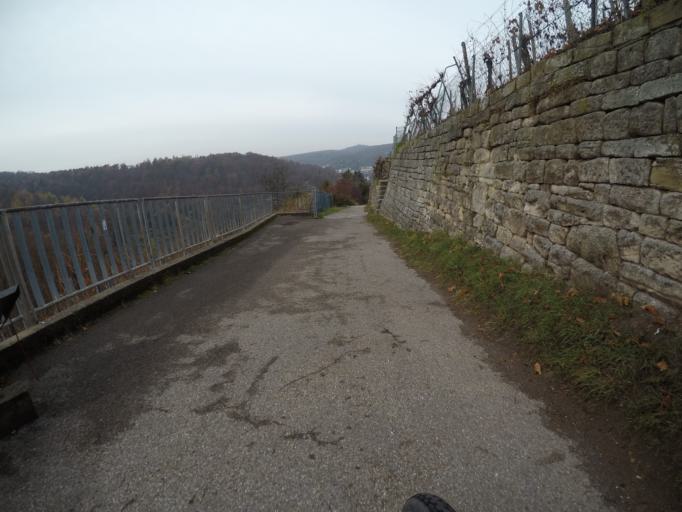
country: DE
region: Baden-Wuerttemberg
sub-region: Regierungsbezirk Stuttgart
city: Stuttgart
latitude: 48.7549
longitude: 9.1659
